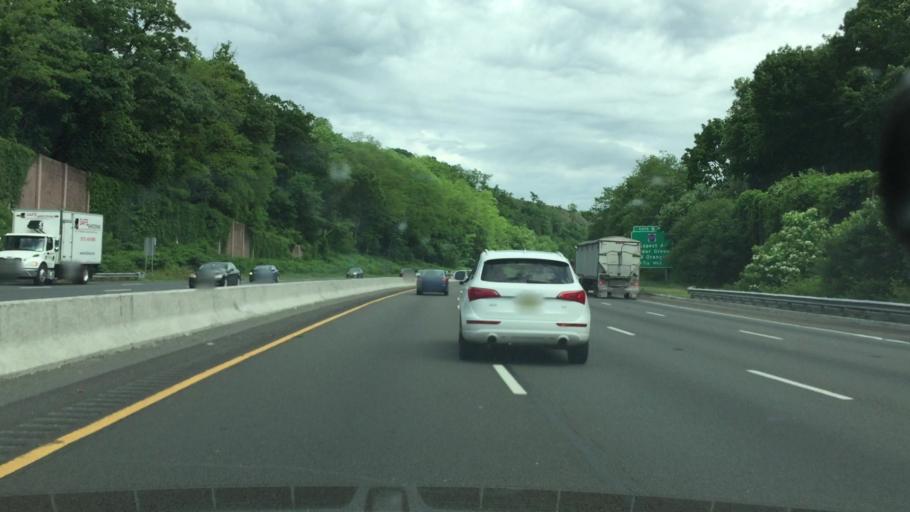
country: US
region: New Jersey
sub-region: Essex County
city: West Orange
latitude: 40.7859
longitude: -74.2456
